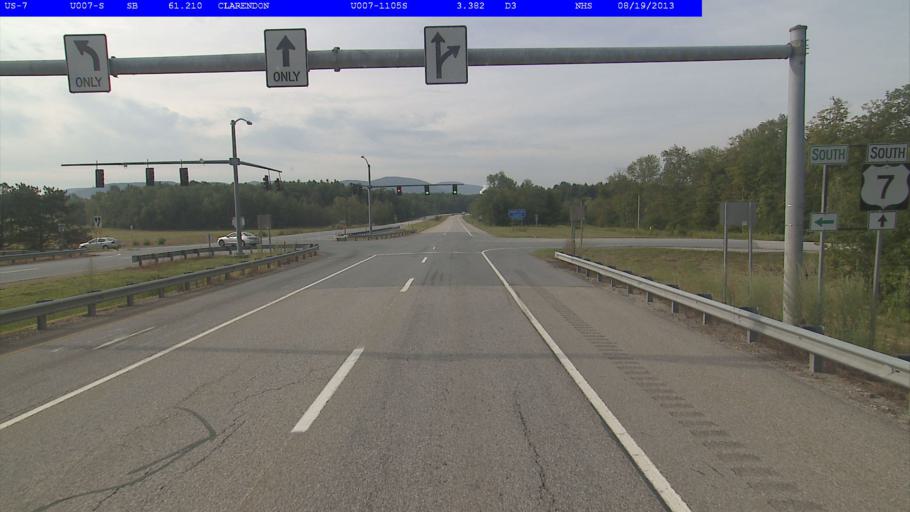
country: US
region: Vermont
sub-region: Rutland County
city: Rutland
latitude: 43.5416
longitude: -72.9584
